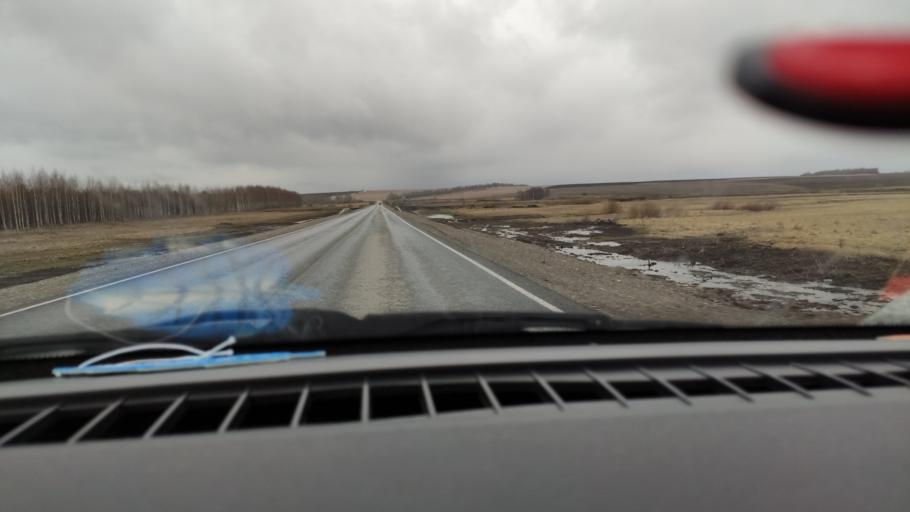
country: RU
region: Tatarstan
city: Cheremshan
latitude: 54.7901
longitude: 51.4535
